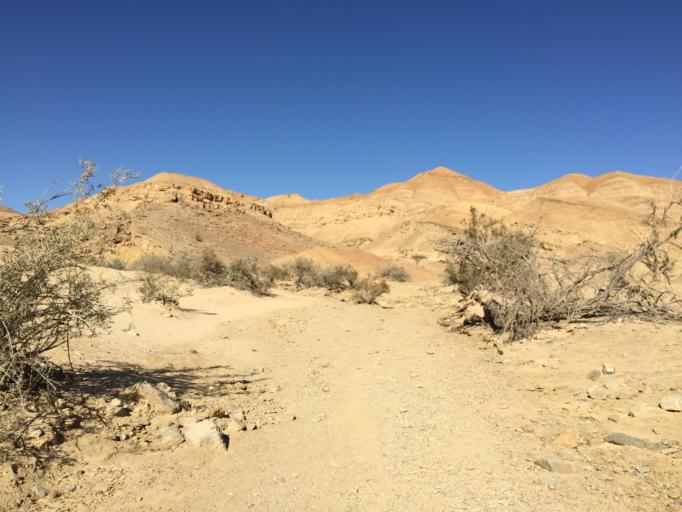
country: IL
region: Southern District
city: Mitzpe Ramon
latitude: 30.6027
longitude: 34.9492
